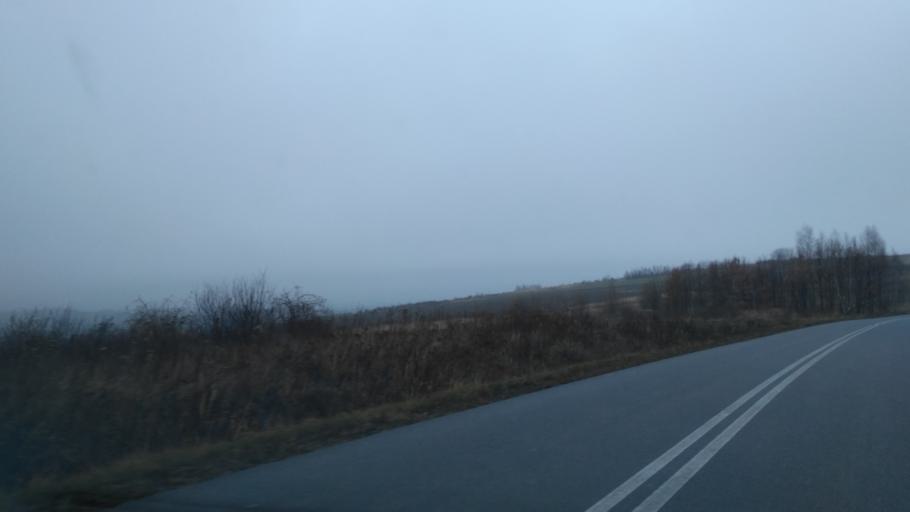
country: PL
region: Subcarpathian Voivodeship
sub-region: Powiat jaroslawski
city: Jodlowka
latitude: 49.8967
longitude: 22.4833
